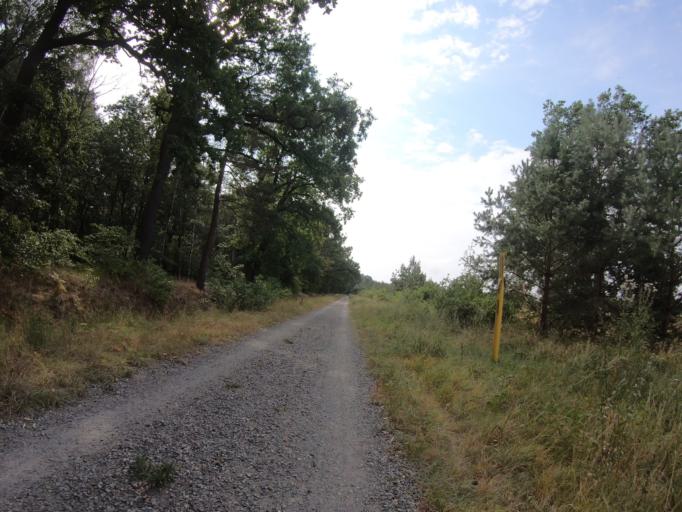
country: DE
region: Lower Saxony
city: Gifhorn
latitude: 52.4554
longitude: 10.5597
